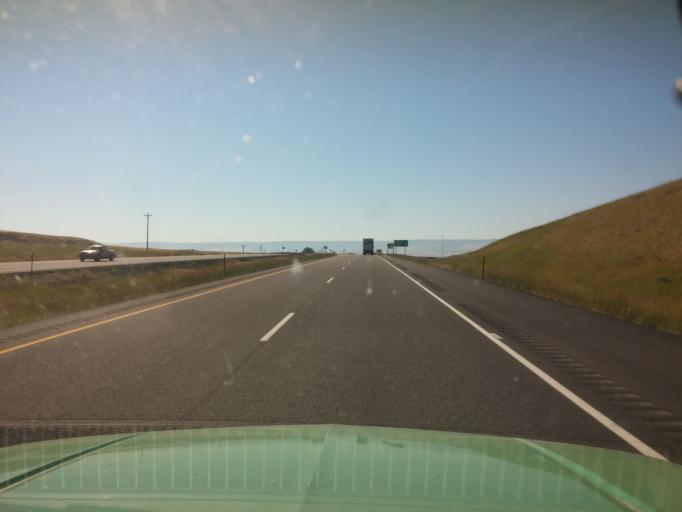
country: US
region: Idaho
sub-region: Nez Perce County
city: Lewiston
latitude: 46.4675
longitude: -117.0276
